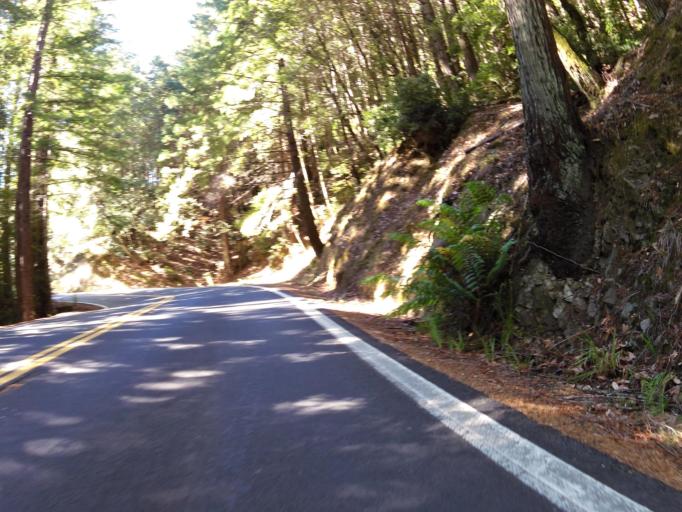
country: US
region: California
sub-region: Humboldt County
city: Redway
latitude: 39.8530
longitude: -123.7297
